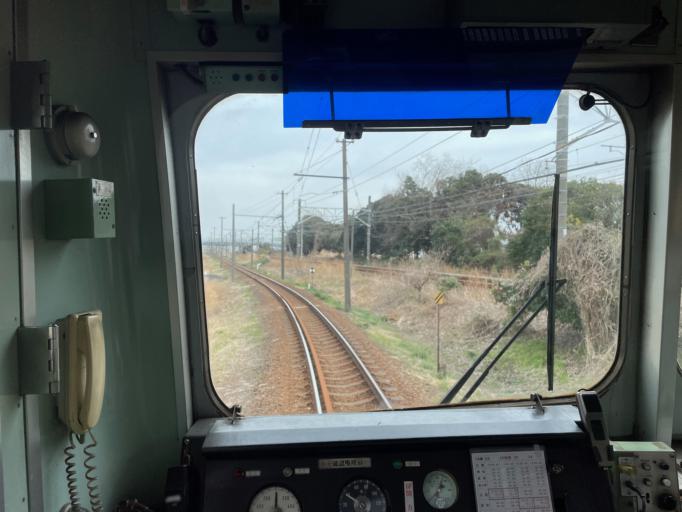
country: JP
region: Shizuoka
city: Fuji
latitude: 35.1459
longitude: 138.6923
